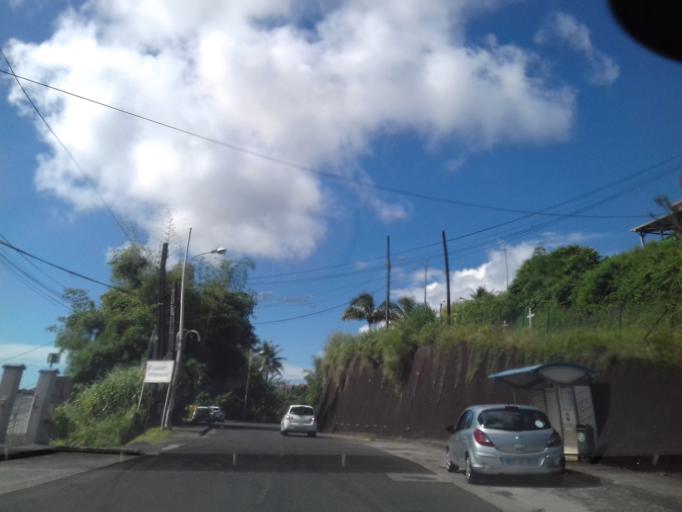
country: MQ
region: Martinique
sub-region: Martinique
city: Saint-Joseph
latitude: 14.6723
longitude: -61.0407
